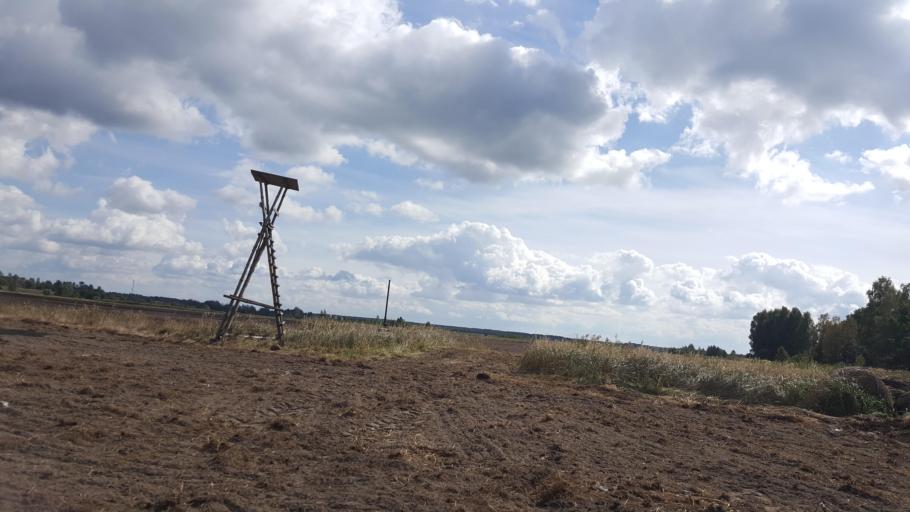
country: BY
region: Brest
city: Kamyanyets
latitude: 52.4597
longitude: 23.9304
